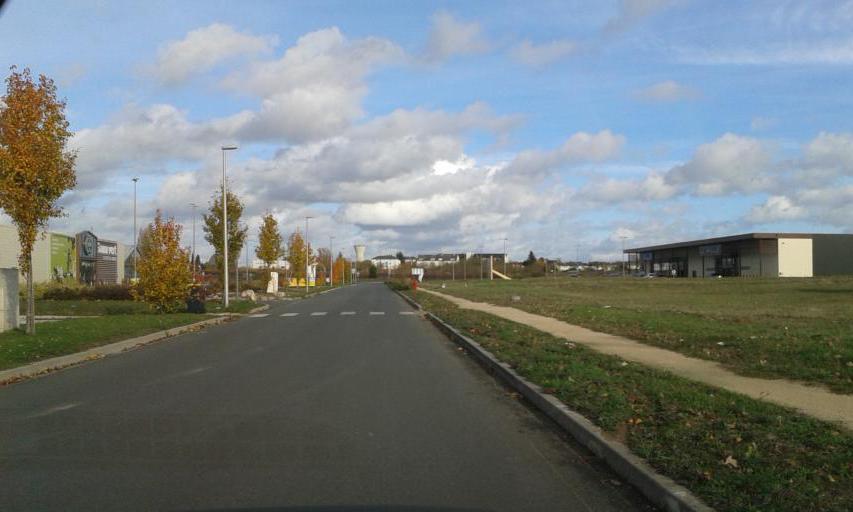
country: FR
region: Centre
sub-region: Departement du Loiret
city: Tavers
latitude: 47.7674
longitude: 1.6141
